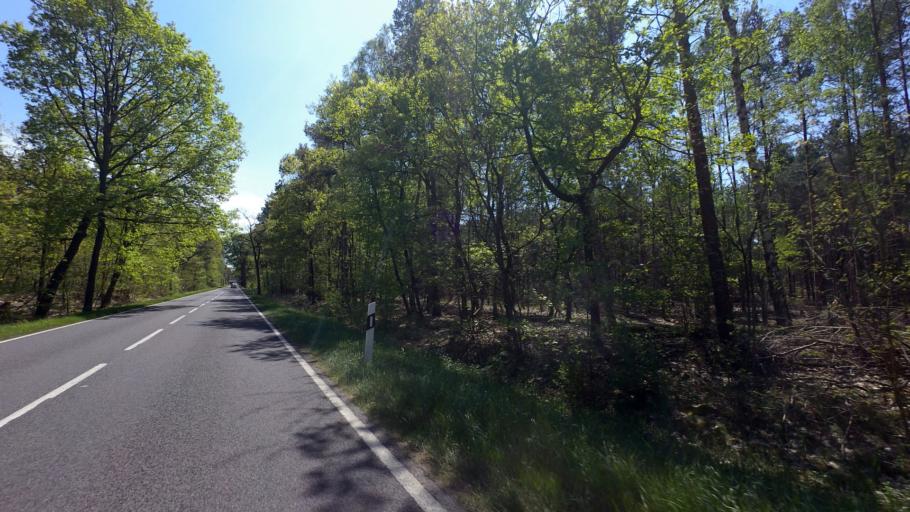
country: DE
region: Brandenburg
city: Gross Koris
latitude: 52.1811
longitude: 13.7098
